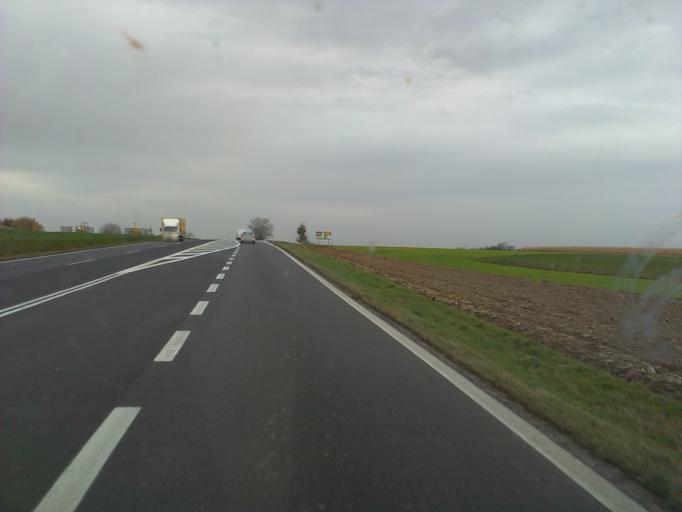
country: PL
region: Subcarpathian Voivodeship
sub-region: Powiat lancucki
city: Kosina
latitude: 50.0705
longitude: 22.3475
